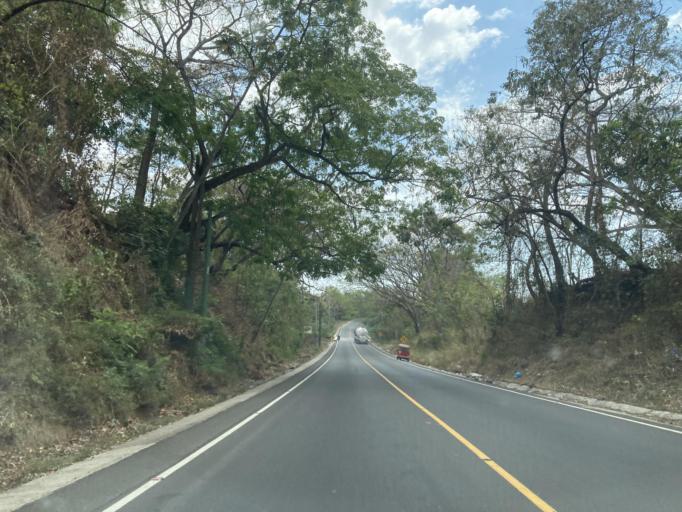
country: GT
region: Santa Rosa
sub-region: Municipio de Taxisco
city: Taxisco
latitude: 14.0845
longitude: -90.4927
